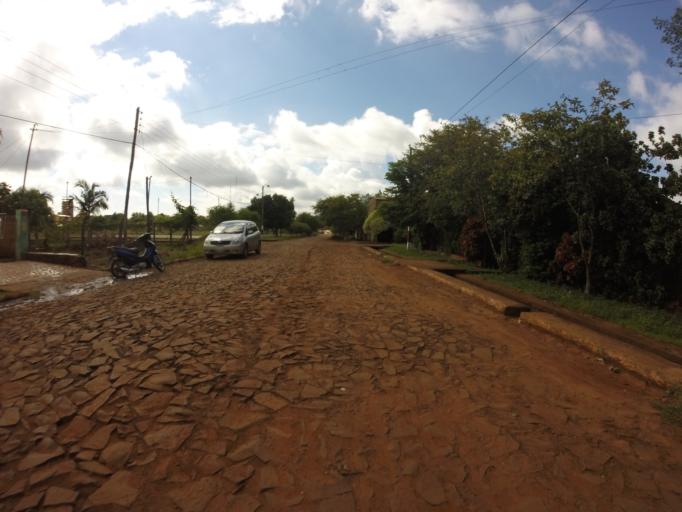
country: PY
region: Alto Parana
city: Ciudad del Este
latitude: -25.3970
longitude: -54.6442
